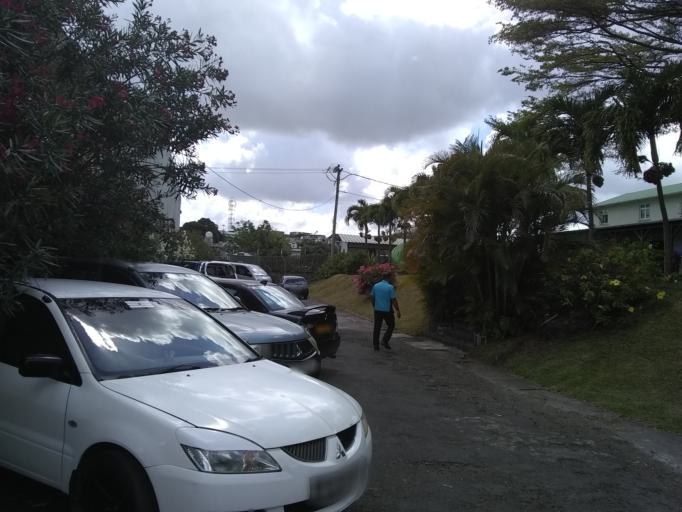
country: MU
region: Plaines Wilhems
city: Quatre Bornes
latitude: -20.2746
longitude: 57.4996
